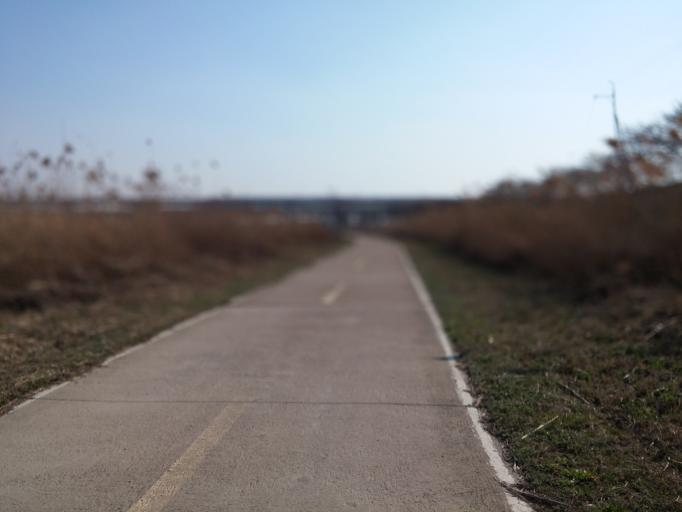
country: KR
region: Chungcheongbuk-do
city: Cheongju-si
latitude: 36.6138
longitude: 127.3419
